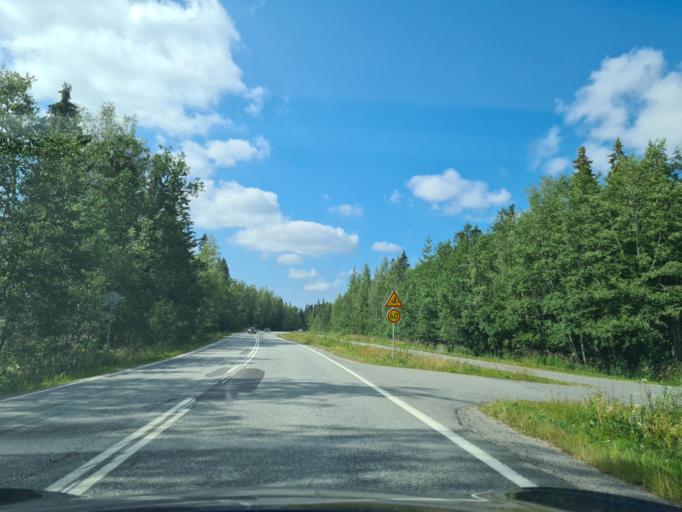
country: FI
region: Ostrobothnia
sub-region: Vaasa
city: Vaasa
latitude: 63.1947
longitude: 21.5523
